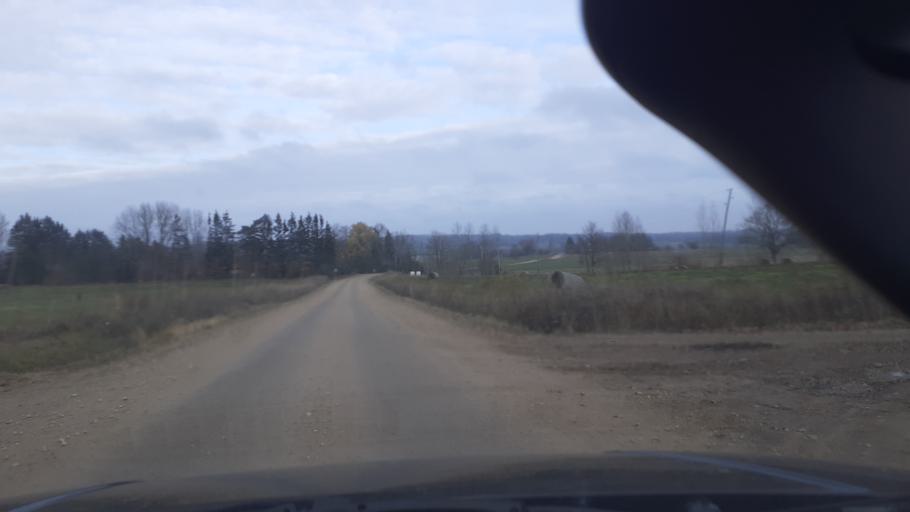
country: LV
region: Aizpute
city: Aizpute
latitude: 56.8626
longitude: 21.6718
